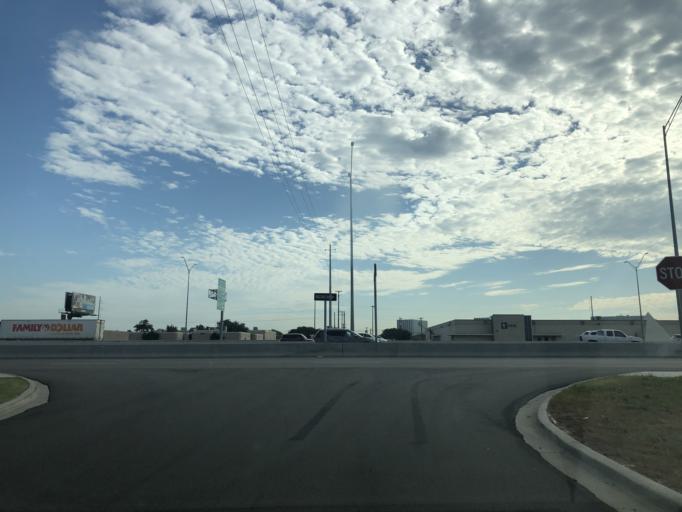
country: US
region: Texas
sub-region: Dallas County
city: Irving
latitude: 32.8239
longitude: -96.8819
